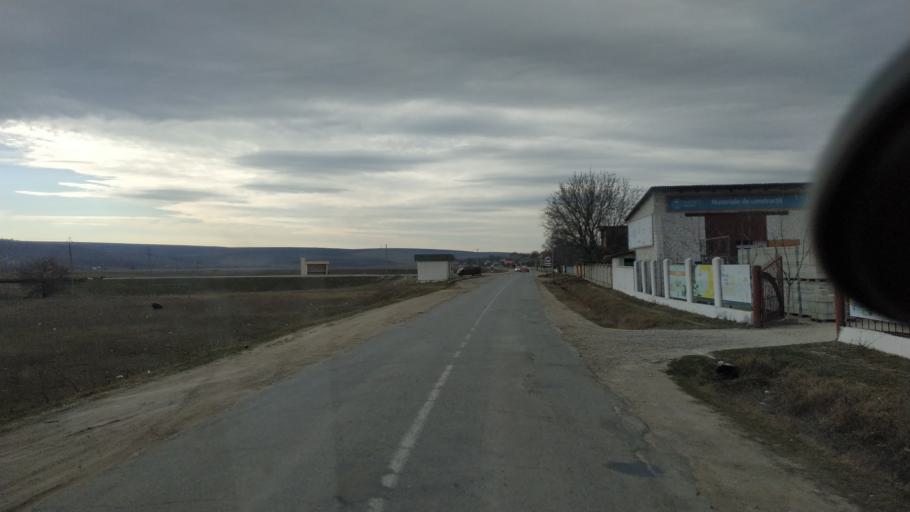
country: MD
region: Chisinau
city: Vadul lui Voda
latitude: 47.1168
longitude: 29.0585
